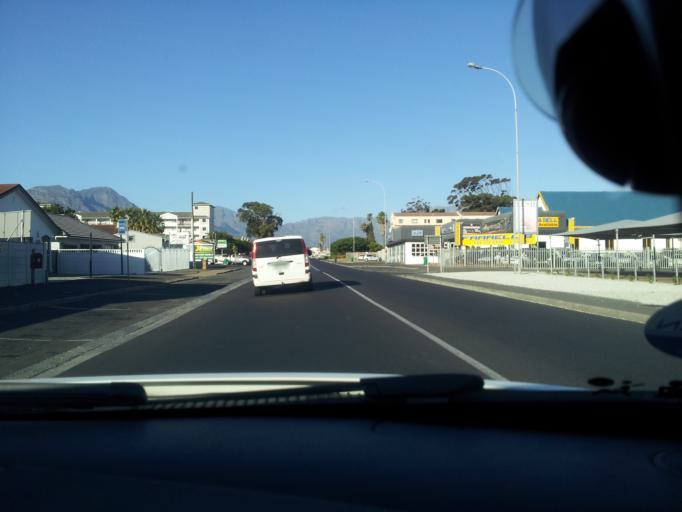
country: ZA
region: Western Cape
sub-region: Cape Winelands District Municipality
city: Stellenbosch
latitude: -34.1104
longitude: 18.8356
